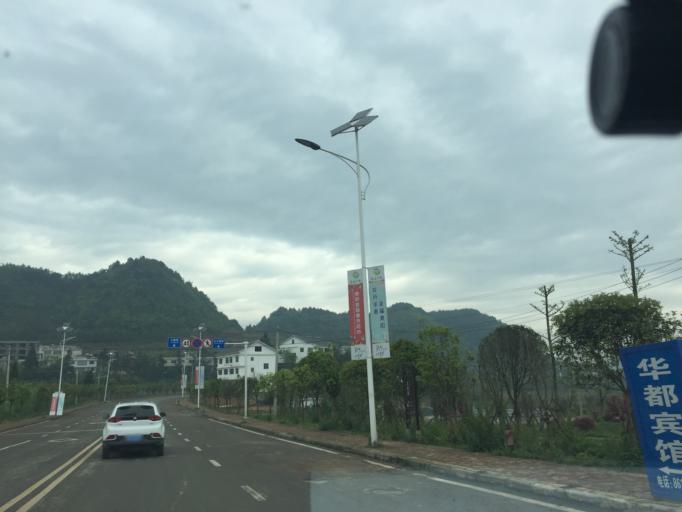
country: CN
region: Guizhou Sheng
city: Guiyang
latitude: 26.8348
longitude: 106.8743
